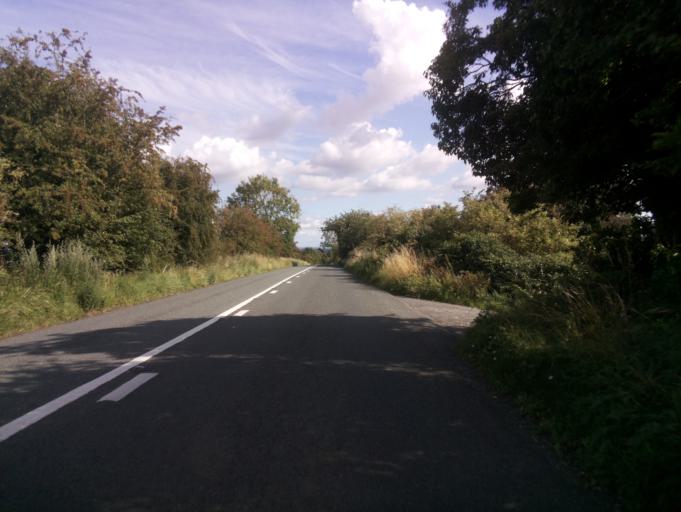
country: GB
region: England
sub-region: Gloucestershire
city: Cirencester
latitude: 51.7389
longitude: -1.9893
